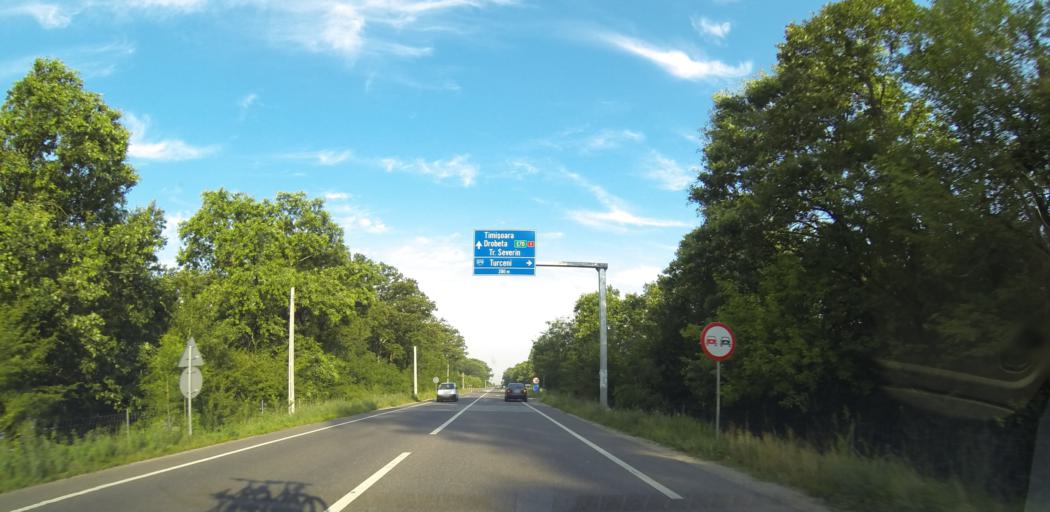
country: RO
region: Gorj
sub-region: Comuna Ionesti
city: Ionesti
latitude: 44.5723
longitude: 23.4304
